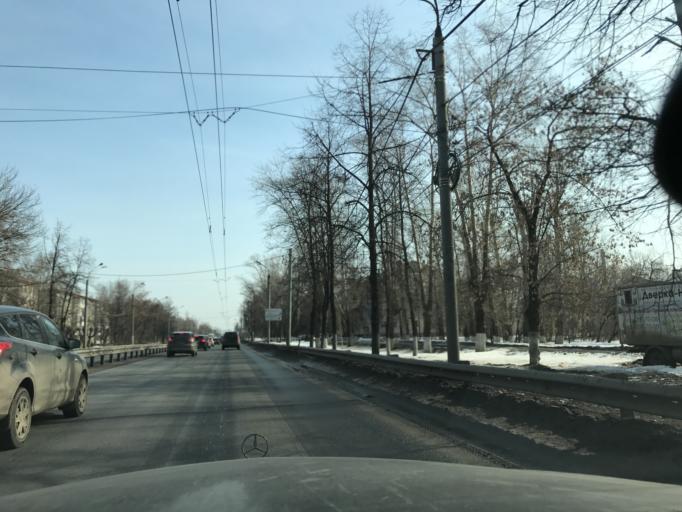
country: RU
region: Nizjnij Novgorod
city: Gorbatovka
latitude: 56.3130
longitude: 43.8532
